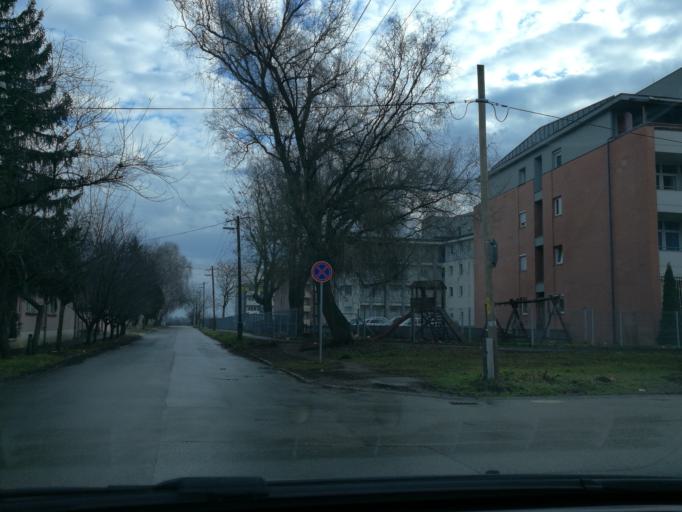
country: HU
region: Szabolcs-Szatmar-Bereg
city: Nyiregyhaza
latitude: 47.9492
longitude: 21.7337
